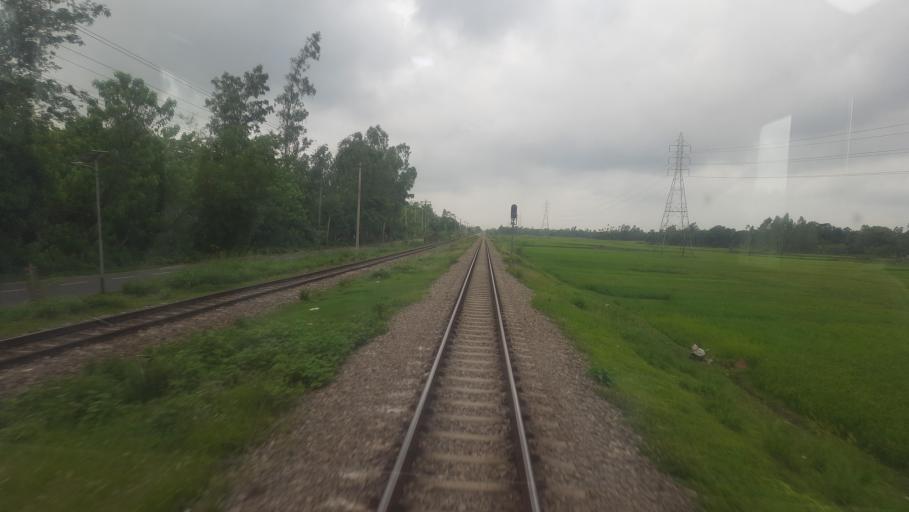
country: BD
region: Dhaka
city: Bhairab Bazar
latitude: 23.9891
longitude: 90.8581
